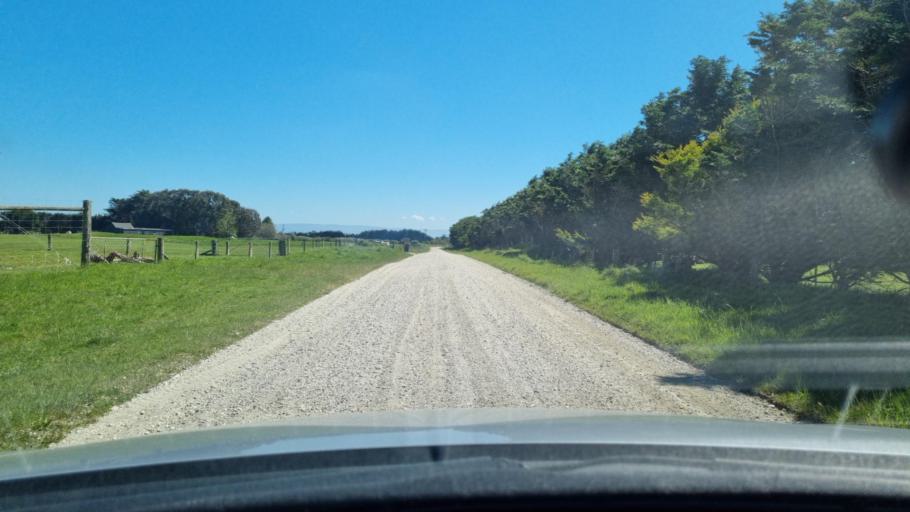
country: NZ
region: Southland
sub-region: Invercargill City
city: Invercargill
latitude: -46.4173
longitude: 168.2672
